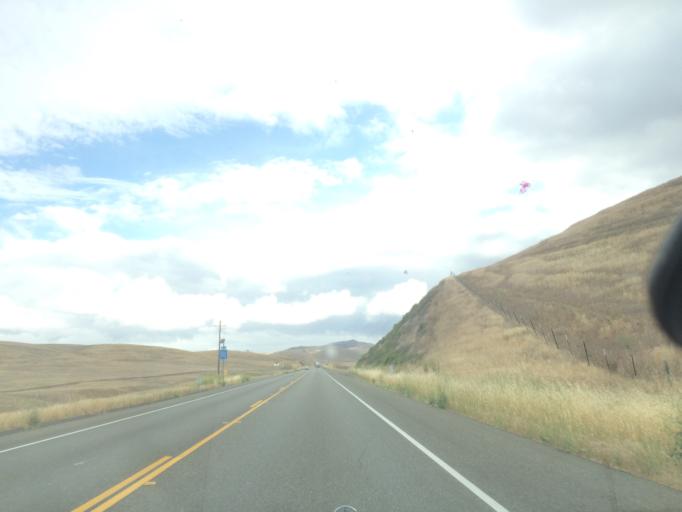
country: US
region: California
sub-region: San Luis Obispo County
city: Shandon
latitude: 35.7509
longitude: -120.2670
